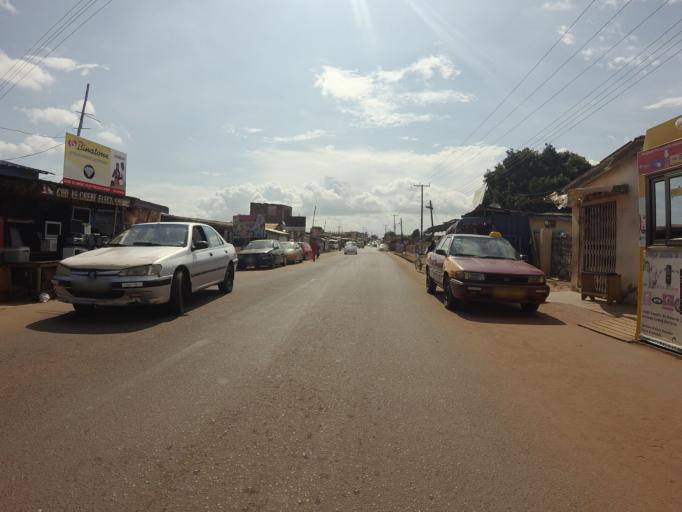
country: GH
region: Greater Accra
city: Medina Estates
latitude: 5.6788
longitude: -0.1760
